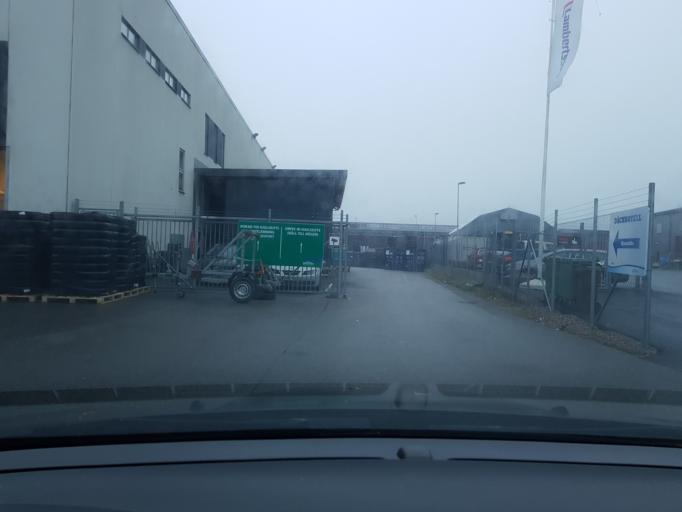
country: SE
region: Uppsala
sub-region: Uppsala Kommun
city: Saevja
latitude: 59.8426
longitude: 17.7285
